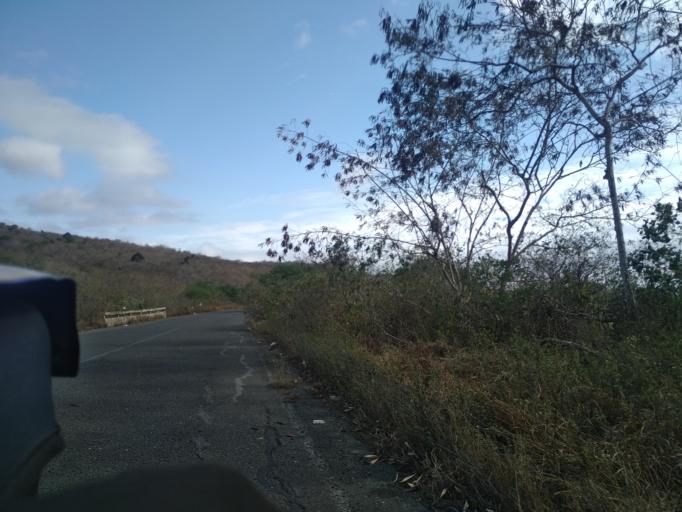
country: EC
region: Manabi
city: Jipijapa
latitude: -1.4564
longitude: -80.7601
